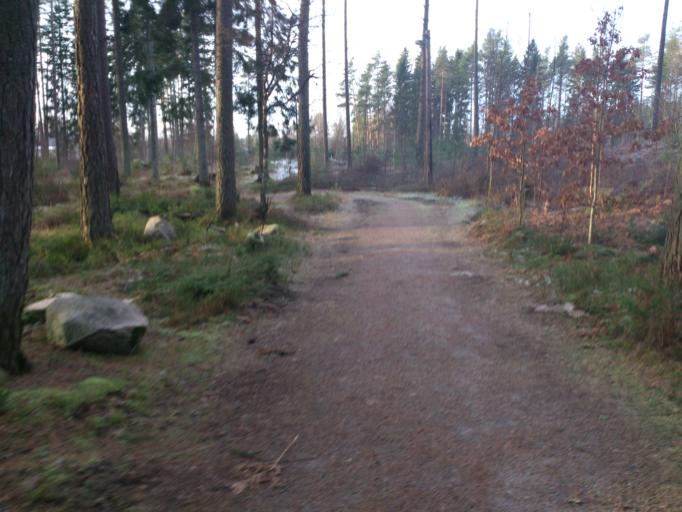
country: SE
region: Kronoberg
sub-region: Alvesta Kommun
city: Moheda
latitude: 56.9976
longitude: 14.5871
